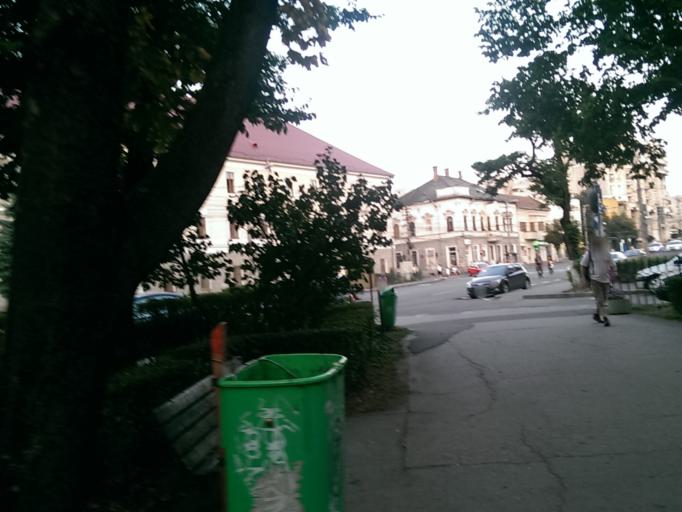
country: RO
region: Cluj
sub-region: Municipiul Cluj-Napoca
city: Cluj-Napoca
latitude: 46.7692
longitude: 23.5984
